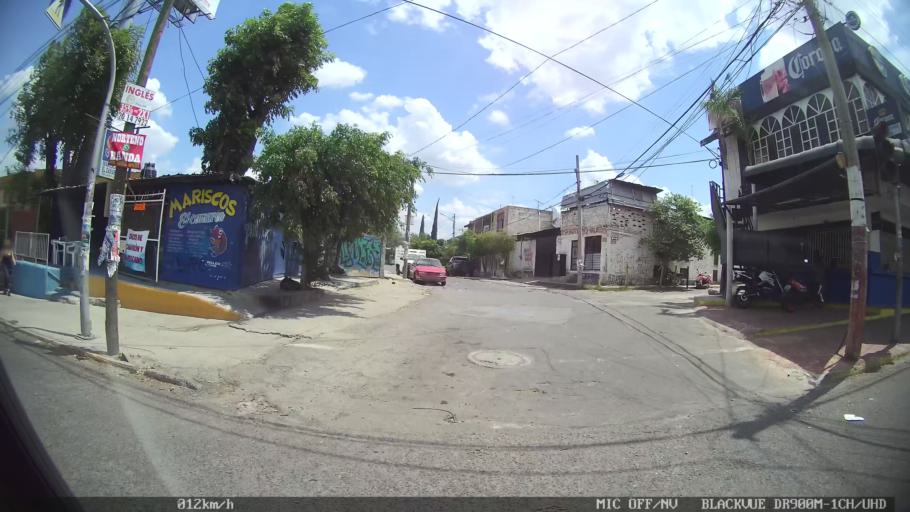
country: MX
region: Jalisco
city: Tlaquepaque
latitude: 20.6323
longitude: -103.2689
